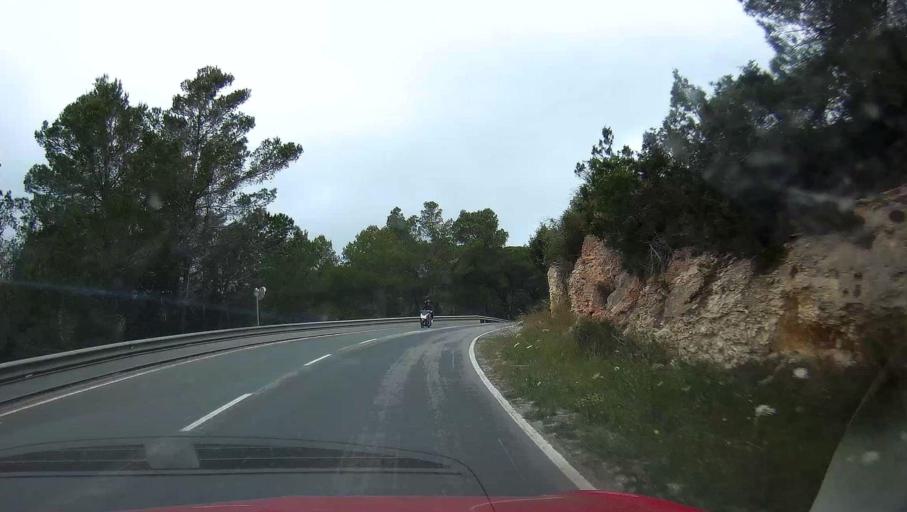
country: ES
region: Balearic Islands
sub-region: Illes Balears
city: Sant Joan de Labritja
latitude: 39.0772
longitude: 1.5026
